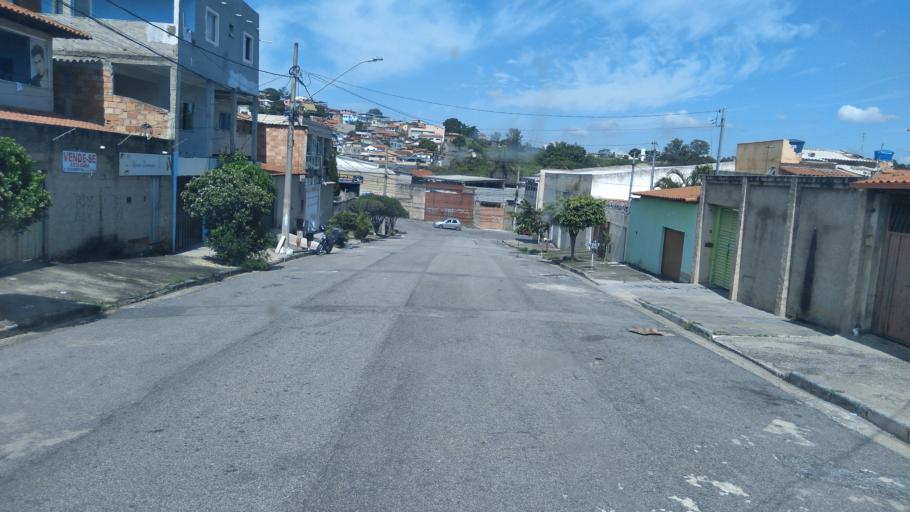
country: BR
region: Minas Gerais
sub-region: Belo Horizonte
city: Belo Horizonte
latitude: -19.8583
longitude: -43.8953
